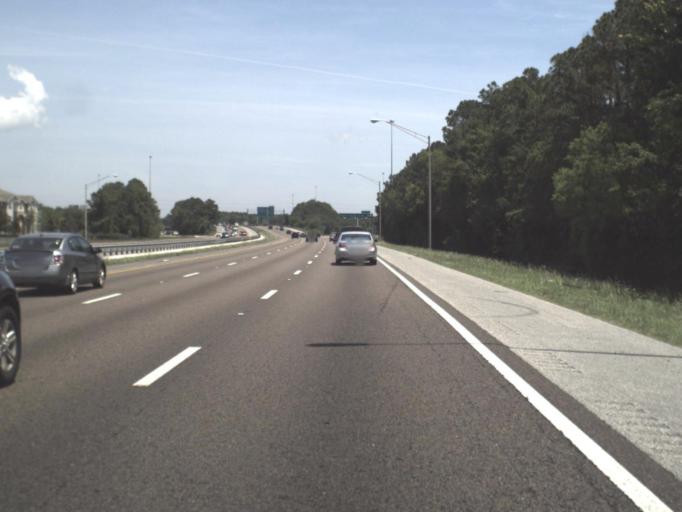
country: US
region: Florida
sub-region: Saint Johns County
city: Fruit Cove
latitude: 30.1707
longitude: -81.6098
